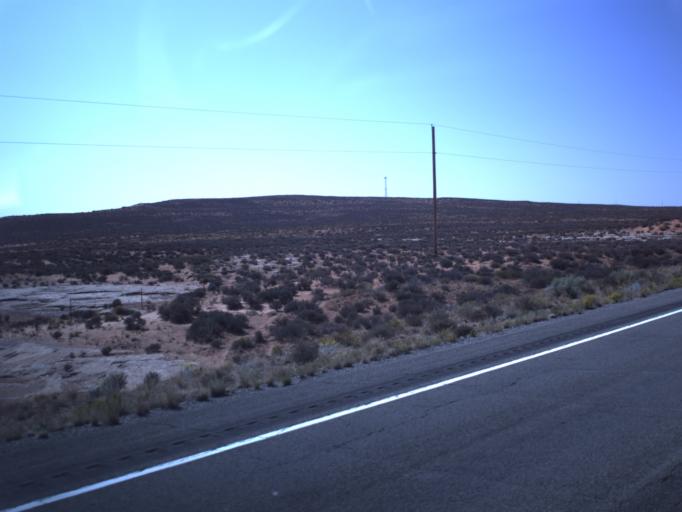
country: US
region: Utah
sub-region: San Juan County
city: Blanding
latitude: 37.0427
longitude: -109.5799
